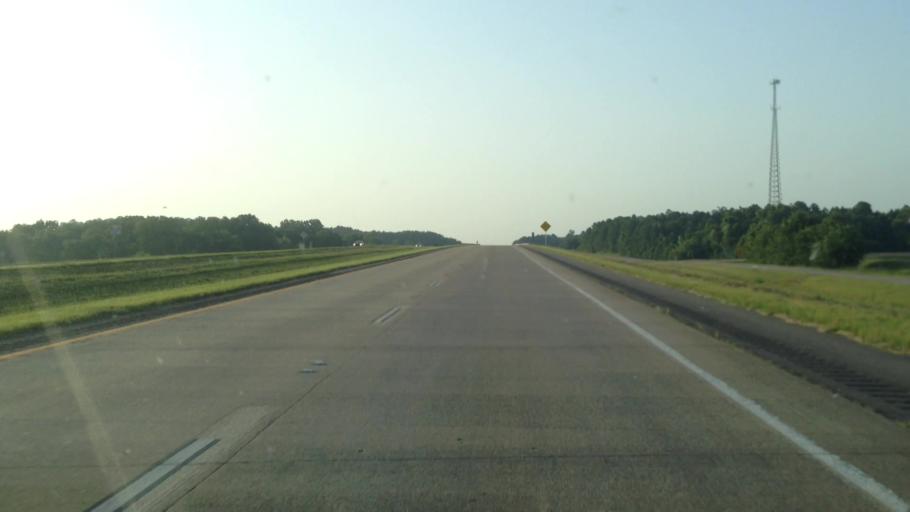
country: US
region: Louisiana
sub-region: Grant Parish
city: Colfax
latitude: 31.4967
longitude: -92.8648
